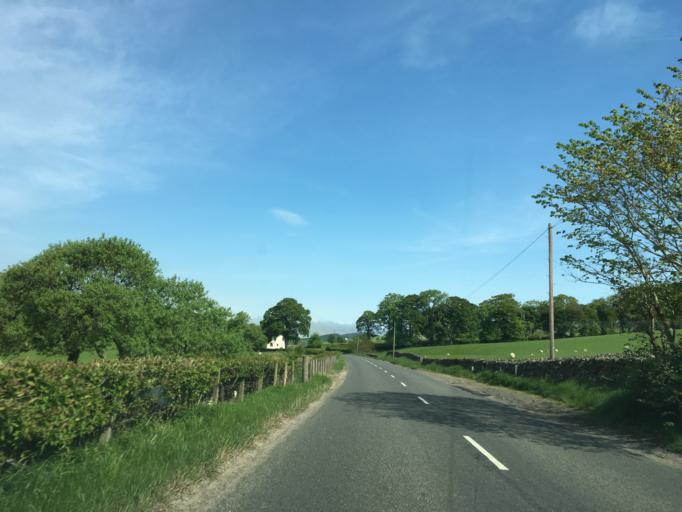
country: GB
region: Scotland
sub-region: South Lanarkshire
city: Biggar
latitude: 55.6246
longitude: -3.4153
